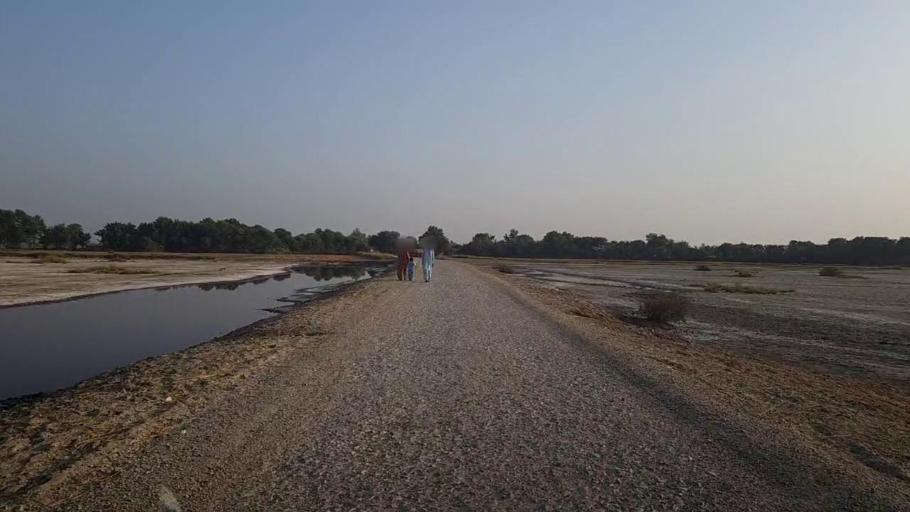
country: PK
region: Sindh
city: Kandhkot
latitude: 28.2436
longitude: 69.0915
